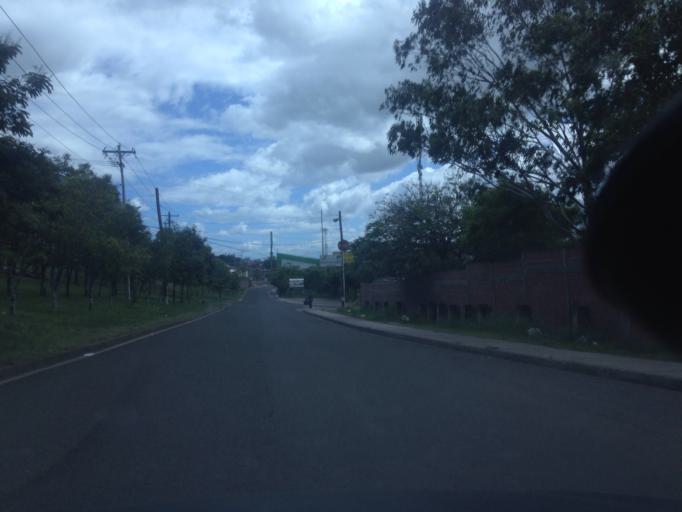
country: HN
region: Francisco Morazan
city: El Tablon
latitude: 14.0671
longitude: -87.1706
